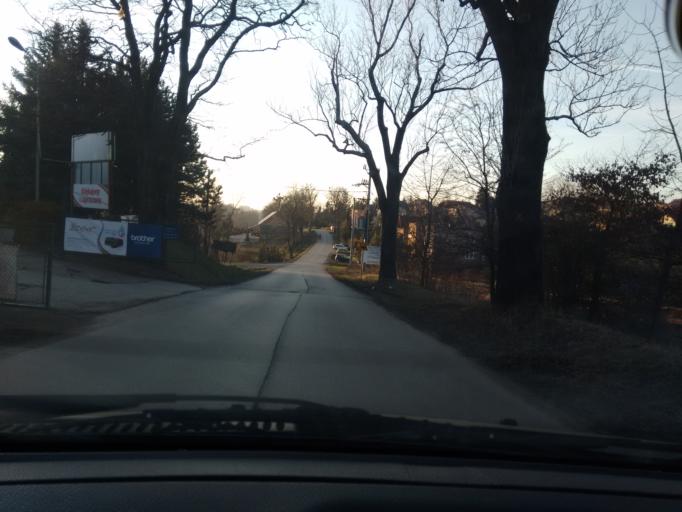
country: PL
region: Silesian Voivodeship
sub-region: Powiat cieszynski
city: Puncow
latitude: 49.7483
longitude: 18.6697
